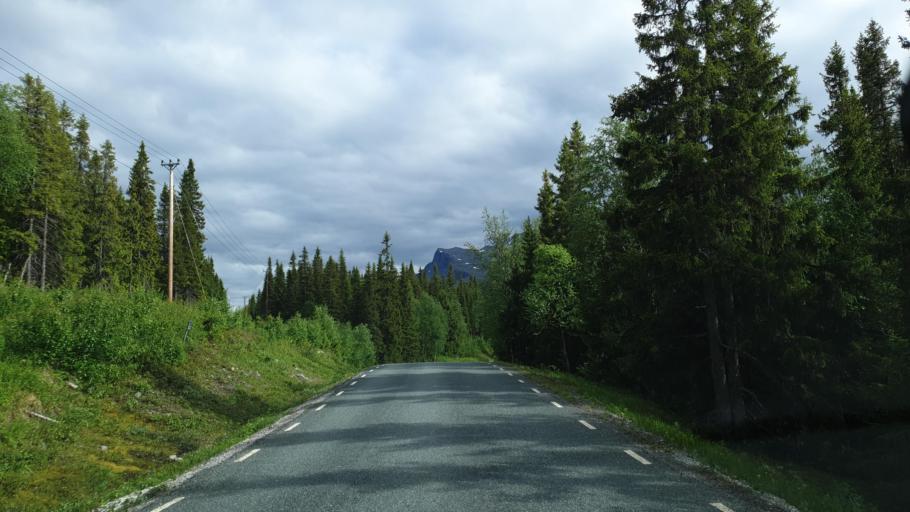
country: SE
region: Vaesterbotten
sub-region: Vilhelmina Kommun
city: Sjoberg
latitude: 65.2641
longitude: 15.3772
